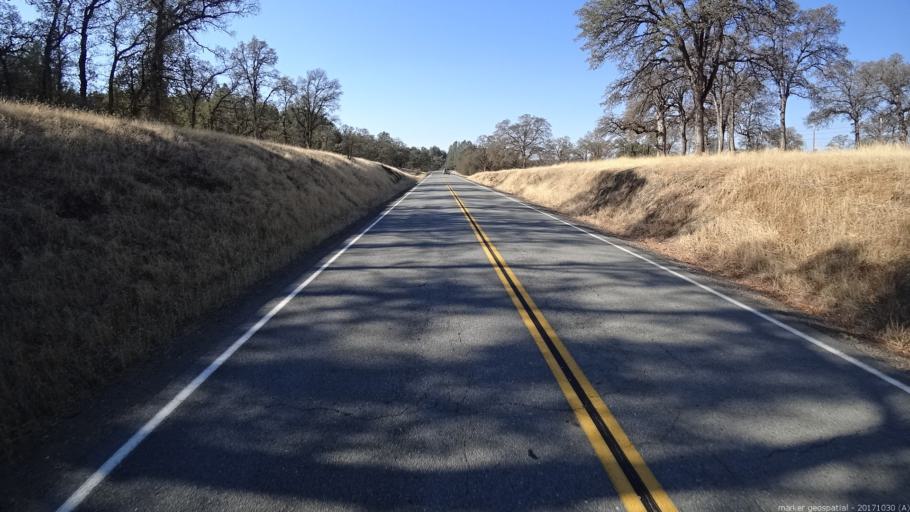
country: US
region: California
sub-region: Shasta County
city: Bella Vista
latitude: 40.6664
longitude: -122.0610
